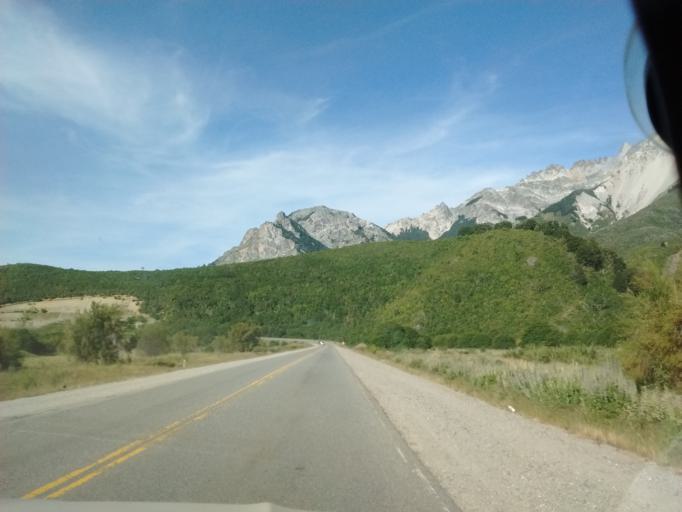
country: AR
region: Rio Negro
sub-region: Departamento de Bariloche
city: San Carlos de Bariloche
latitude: -41.5225
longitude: -71.4585
